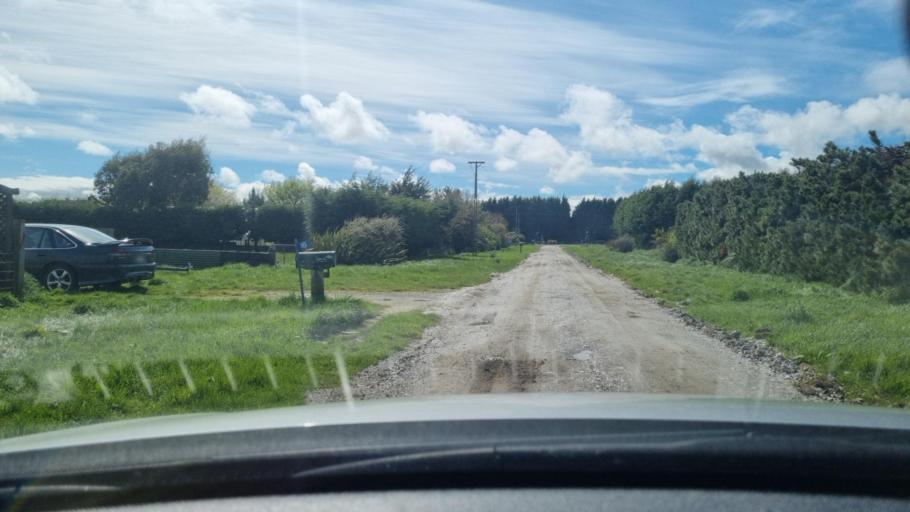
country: NZ
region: Southland
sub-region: Invercargill City
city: Invercargill
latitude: -46.4772
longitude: 168.3914
